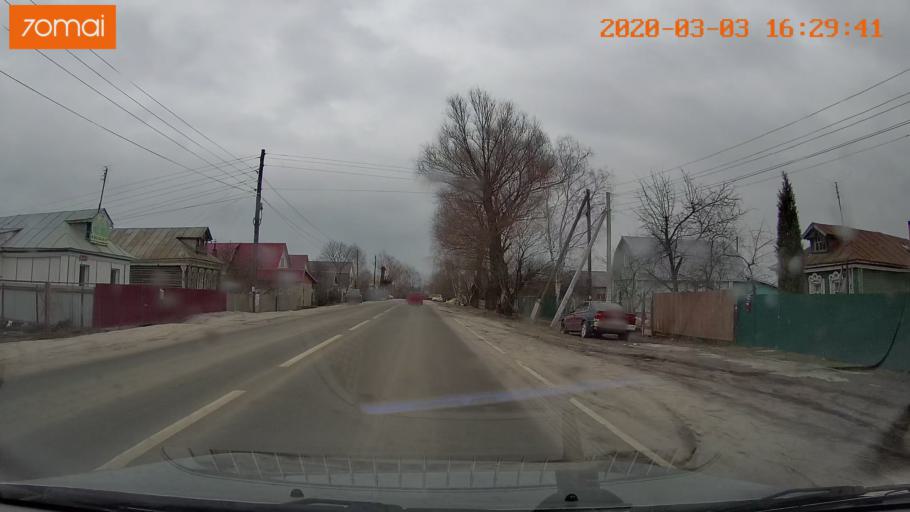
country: RU
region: Moskovskaya
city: Konobeyevo
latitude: 55.4362
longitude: 38.7033
